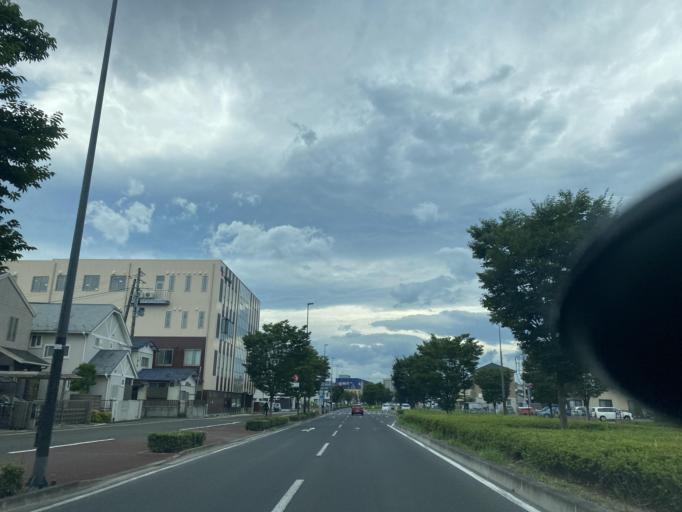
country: JP
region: Miyagi
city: Sendai
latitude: 38.2255
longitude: 140.8926
